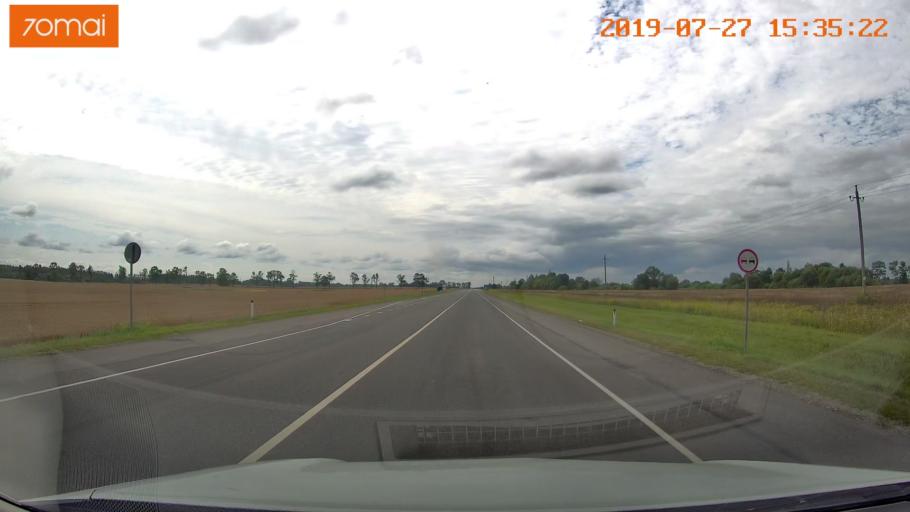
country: RU
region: Kaliningrad
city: Nesterov
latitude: 54.6137
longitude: 22.3990
